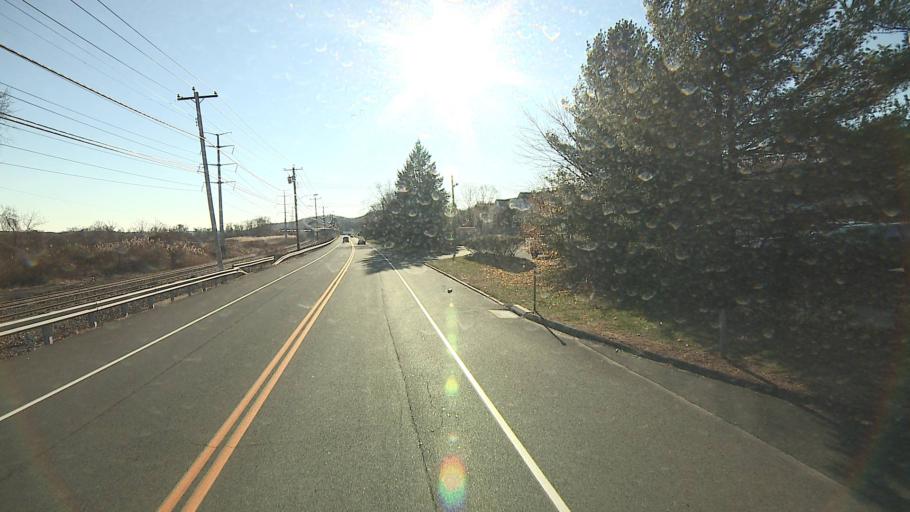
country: US
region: Connecticut
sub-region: New Haven County
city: Hamden
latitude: 41.3479
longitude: -72.8935
